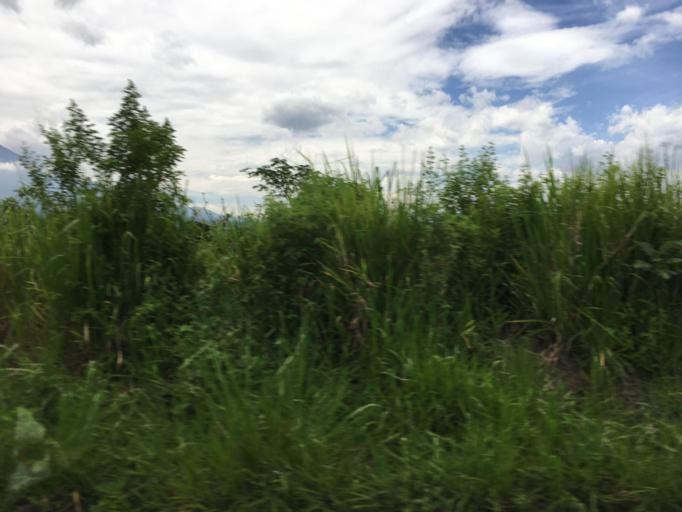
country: GT
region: Escuintla
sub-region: Municipio de Escuintla
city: Escuintla
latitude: 14.3622
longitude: -90.8108
